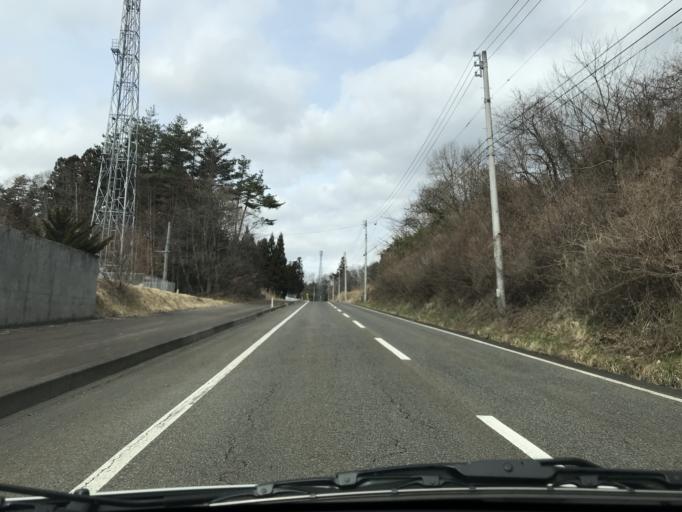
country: JP
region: Iwate
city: Tono
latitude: 39.2934
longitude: 141.3307
